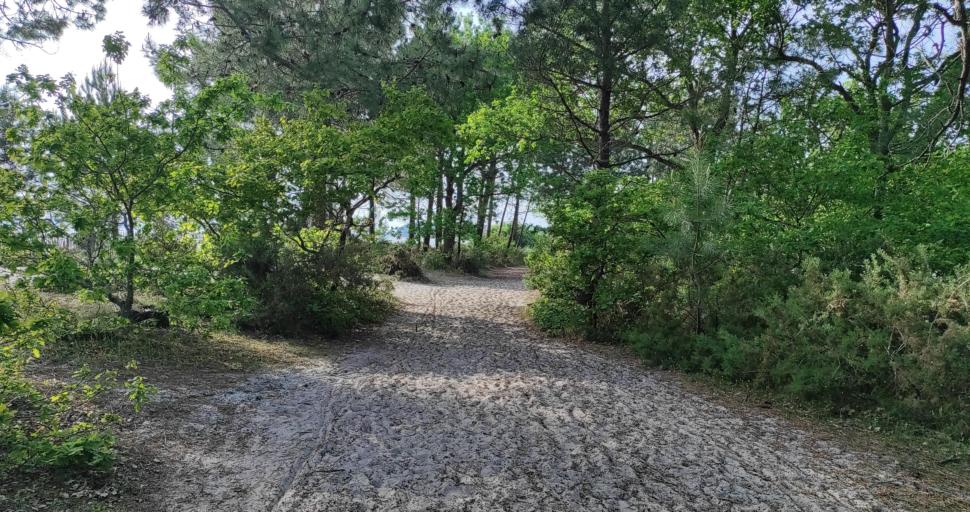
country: FR
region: Aquitaine
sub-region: Departement de la Gironde
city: Andernos-les-Bains
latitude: 44.7453
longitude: -1.1184
